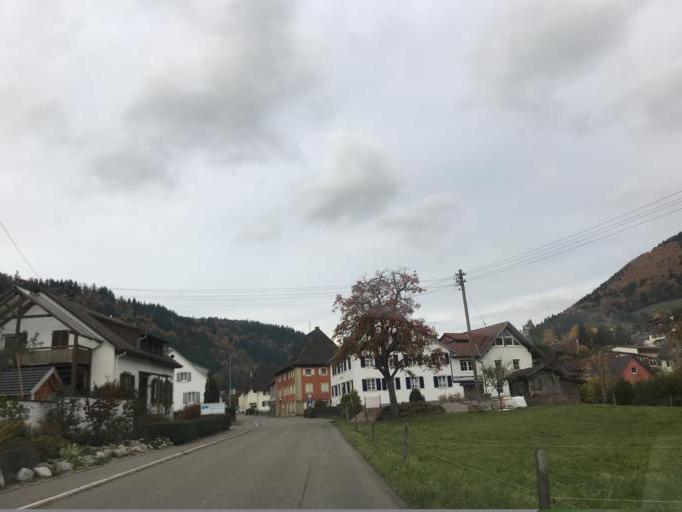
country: DE
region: Baden-Wuerttemberg
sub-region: Freiburg Region
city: Muenstertal/Schwarzwald
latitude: 47.8590
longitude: 7.7956
